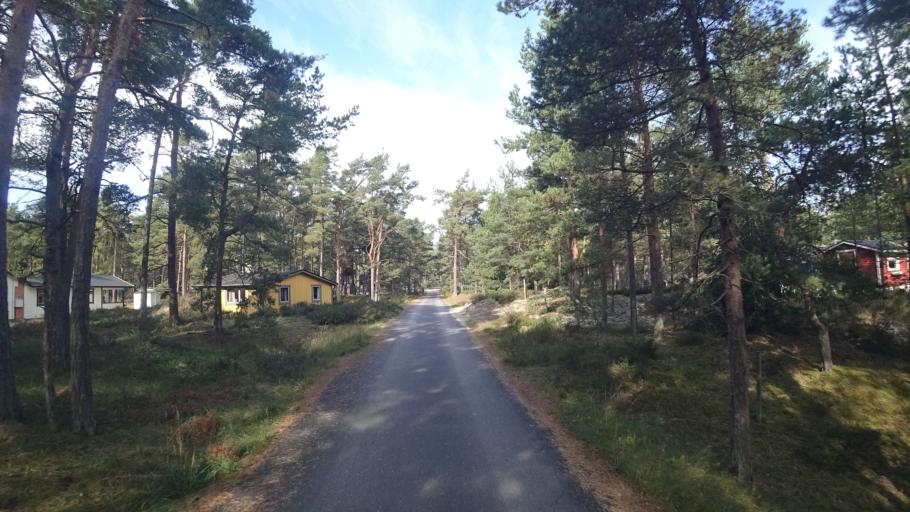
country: SE
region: Skane
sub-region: Kristianstads Kommun
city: Ahus
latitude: 55.9095
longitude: 14.2950
